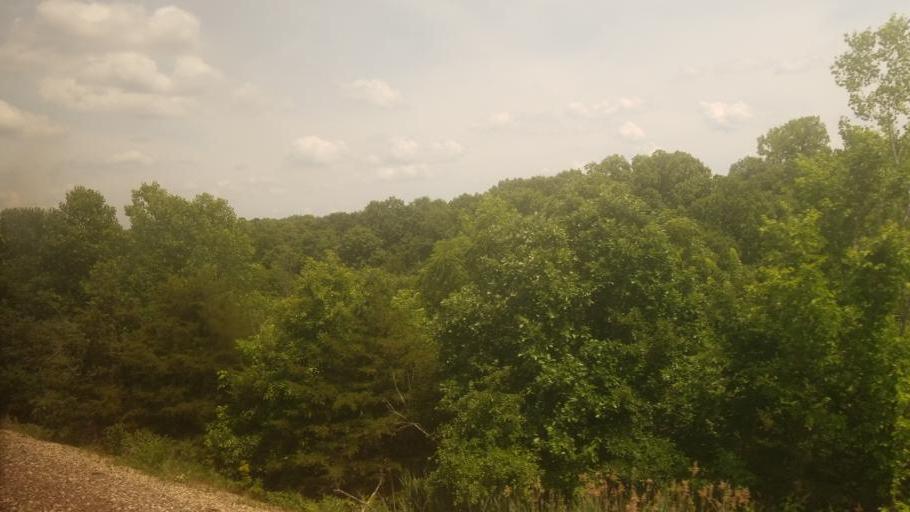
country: US
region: Missouri
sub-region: Clark County
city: Kahoka
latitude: 40.4823
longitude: -91.6963
